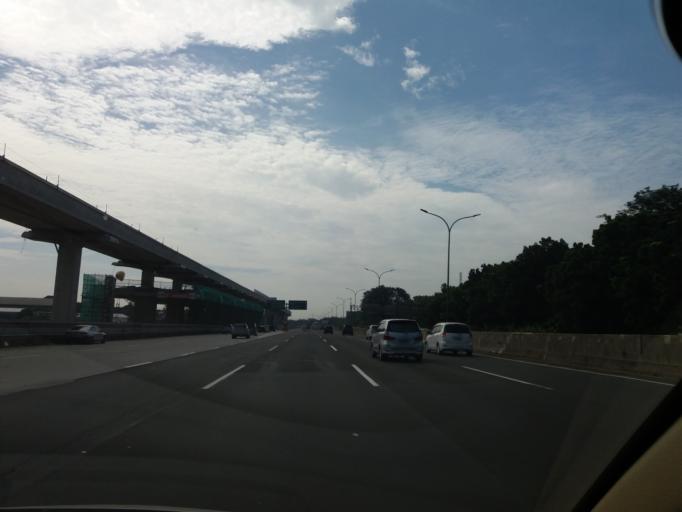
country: ID
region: West Java
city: Cileungsir
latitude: -6.3251
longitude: 106.8869
